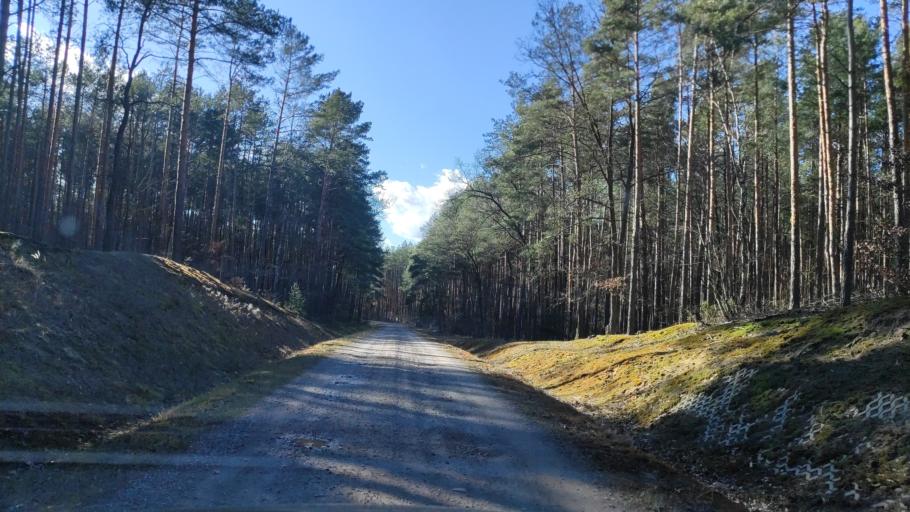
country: PL
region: Masovian Voivodeship
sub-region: Powiat radomski
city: Jastrzebia
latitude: 51.4746
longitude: 21.2591
